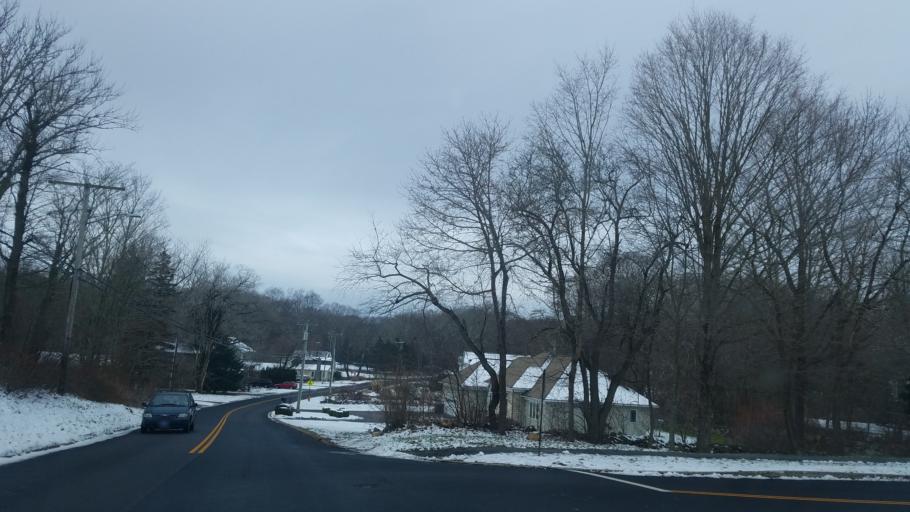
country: US
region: Connecticut
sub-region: New London County
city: Central Waterford
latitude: 41.3473
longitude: -72.1567
